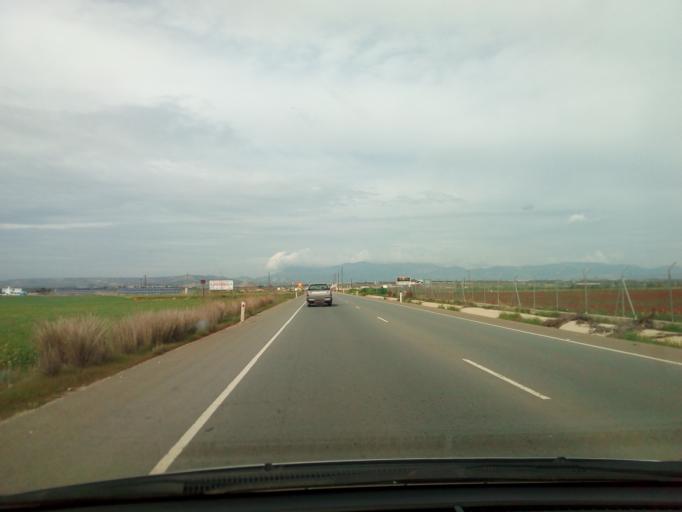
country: CY
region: Lefkosia
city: Akaki
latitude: 35.1429
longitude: 33.1561
